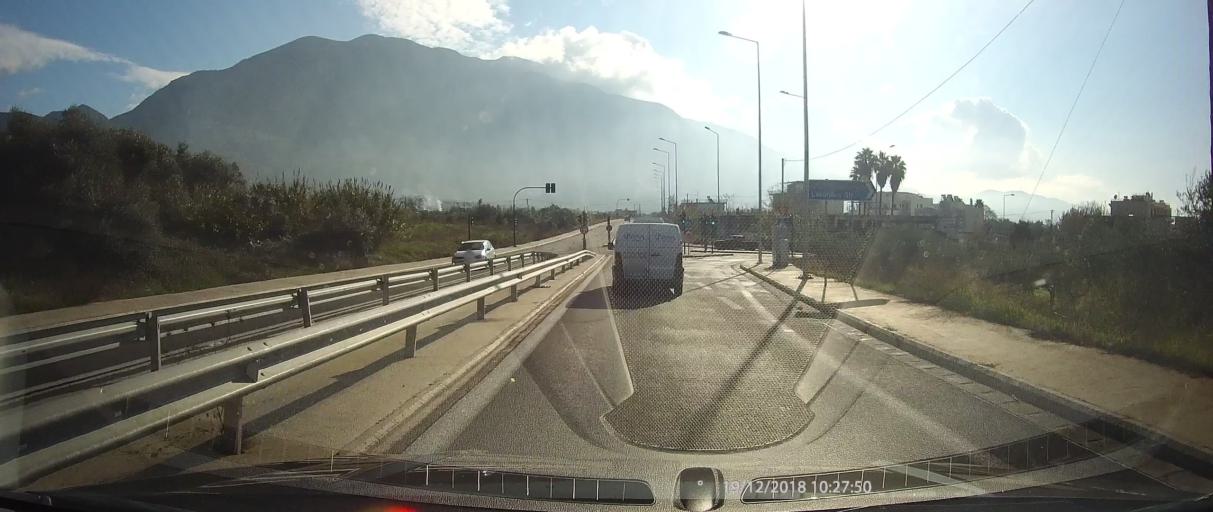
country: GR
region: Peloponnese
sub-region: Nomos Messinias
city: Kalamata
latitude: 37.0311
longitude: 22.1371
